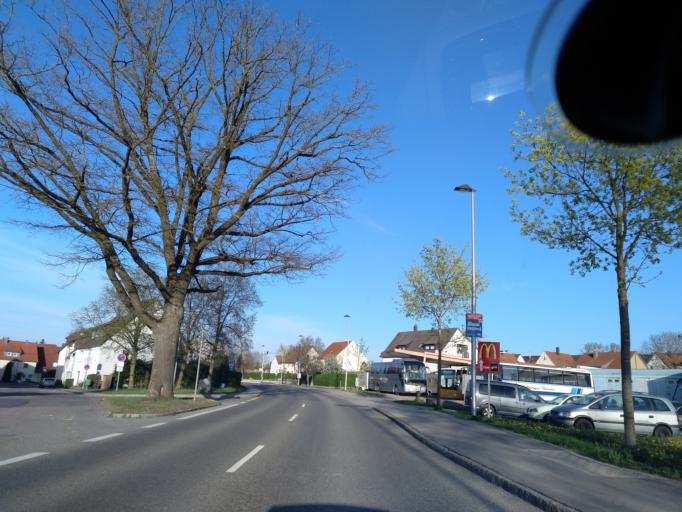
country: DE
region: Baden-Wuerttemberg
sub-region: Regierungsbezirk Stuttgart
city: Crailsheim
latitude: 49.1386
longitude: 10.0224
